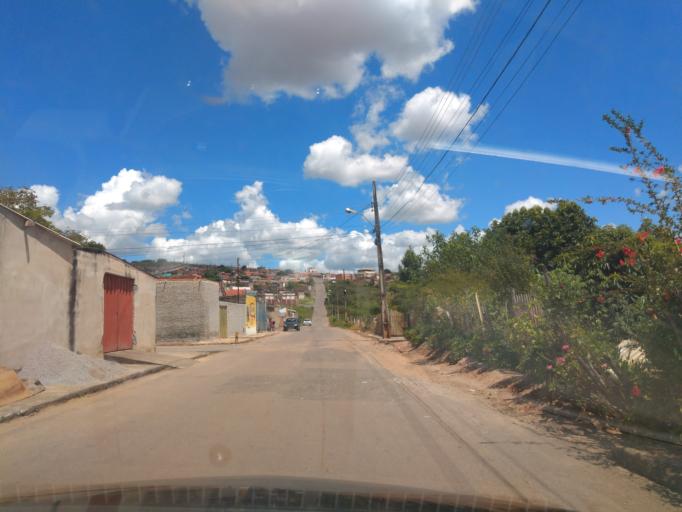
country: BR
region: Minas Gerais
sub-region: Tres Coracoes
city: Tres Coracoes
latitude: -21.6797
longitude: -45.2469
